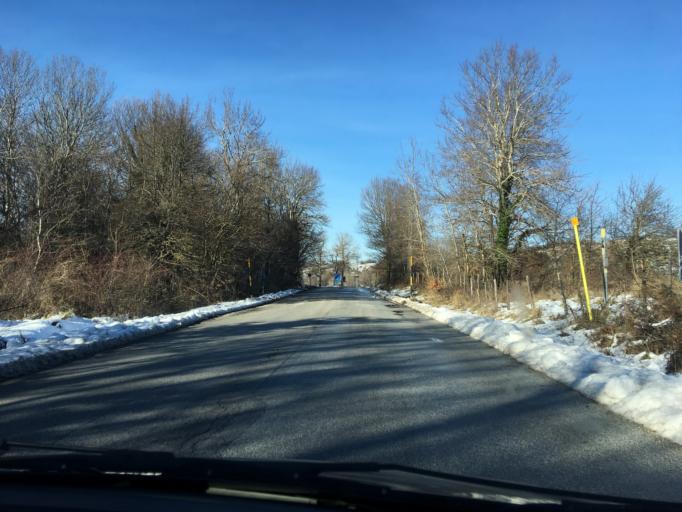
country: IT
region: Abruzzo
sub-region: Provincia di Chieti
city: Rosello
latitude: 41.8621
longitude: 14.3531
